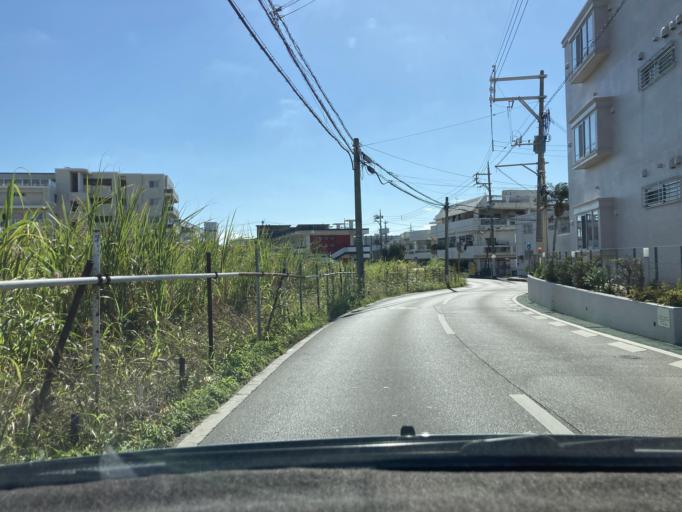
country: JP
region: Okinawa
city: Okinawa
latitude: 26.3551
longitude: 127.8246
